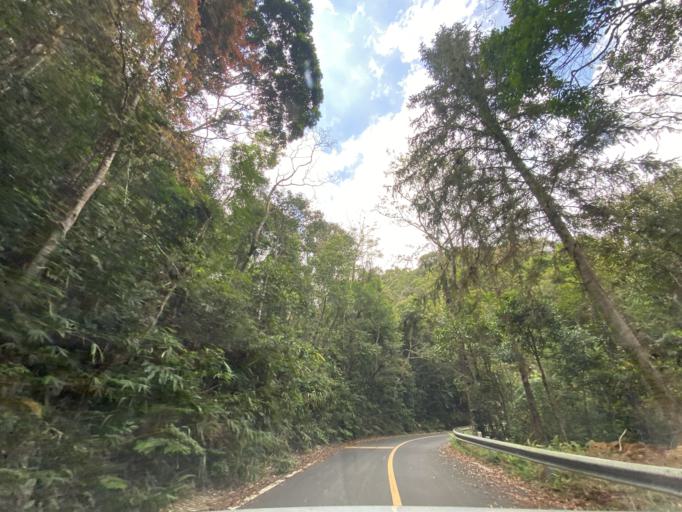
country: CN
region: Hainan
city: Diaoluoshan
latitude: 18.7019
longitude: 109.8823
